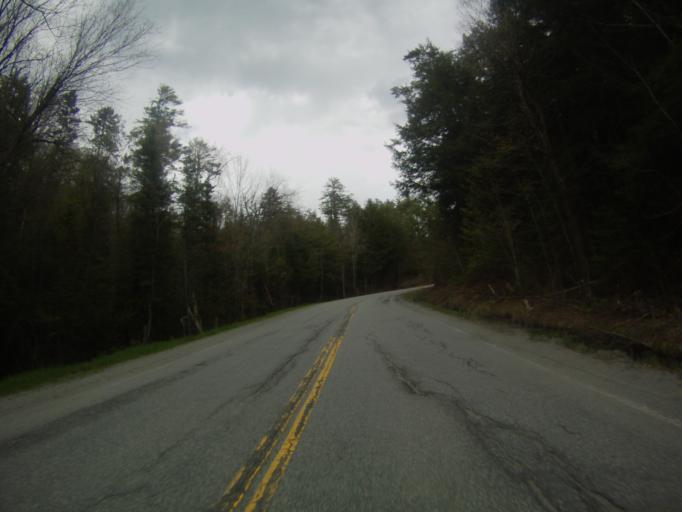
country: US
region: New York
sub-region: Essex County
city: Mineville
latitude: 44.0772
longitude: -73.6252
